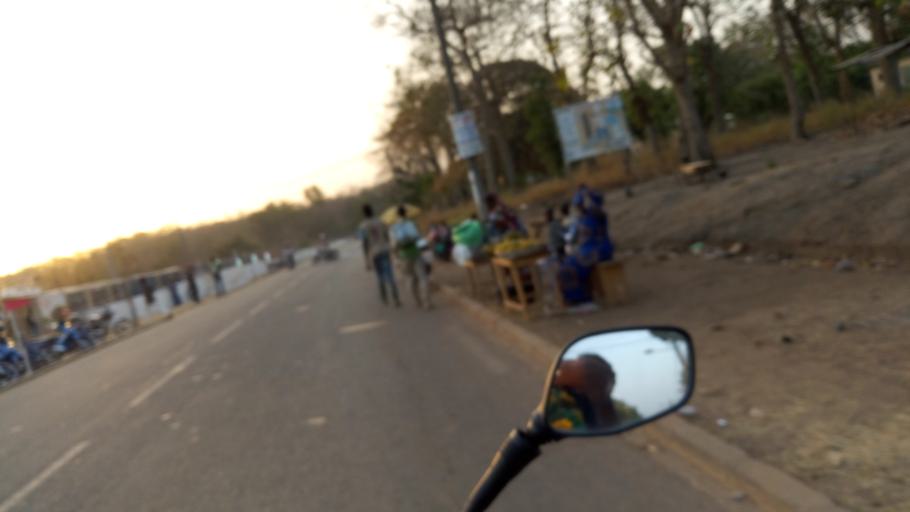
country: TG
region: Kara
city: Kara
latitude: 9.5492
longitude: 1.1820
